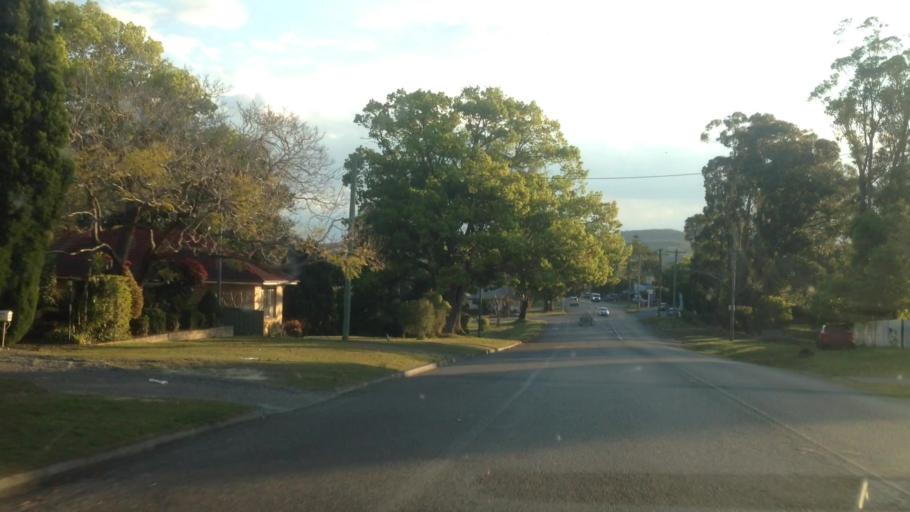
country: AU
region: New South Wales
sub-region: Lake Macquarie Shire
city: Cooranbong
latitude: -33.0687
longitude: 151.4653
